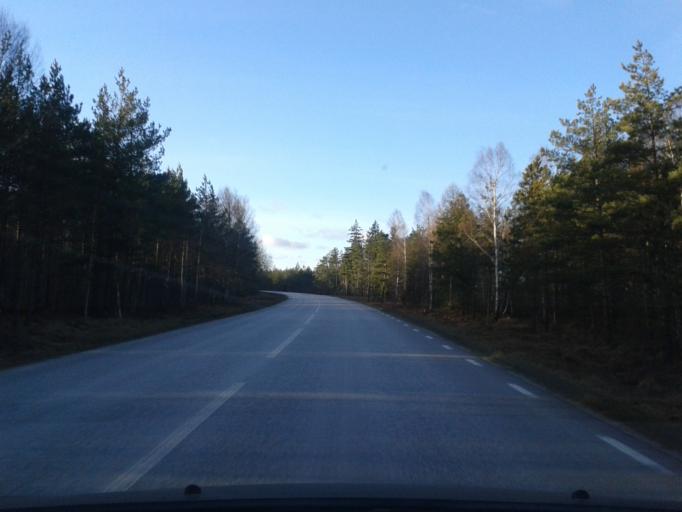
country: SE
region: Gotland
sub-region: Gotland
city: Slite
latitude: 57.4361
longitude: 18.6646
